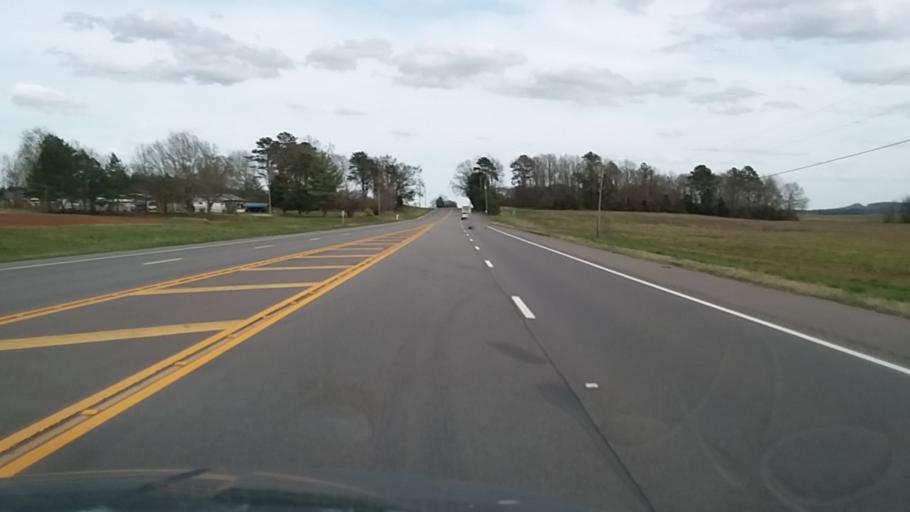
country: US
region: Alabama
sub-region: Lawrence County
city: Town Creek
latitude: 34.6821
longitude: -87.4444
